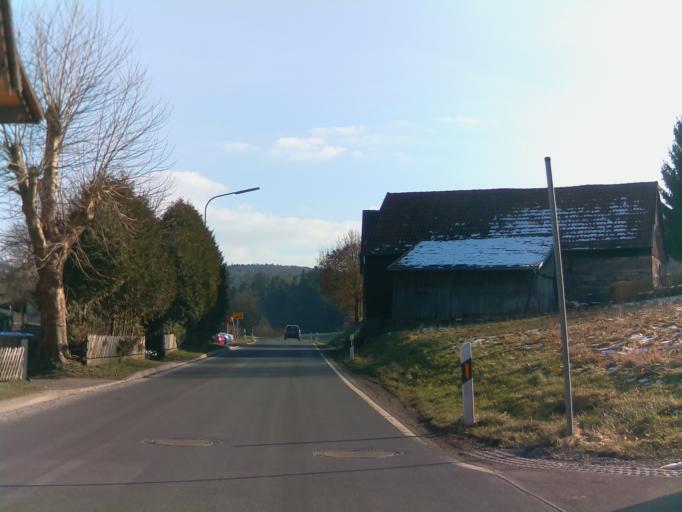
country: DE
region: Bavaria
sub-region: Regierungsbezirk Unterfranken
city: Motten
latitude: 50.4373
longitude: 9.7338
